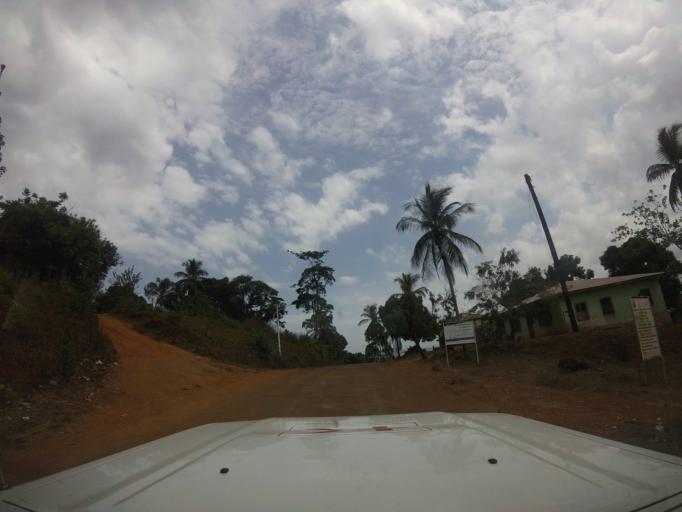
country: LR
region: Grand Cape Mount
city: Robertsport
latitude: 6.7525
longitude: -11.3631
